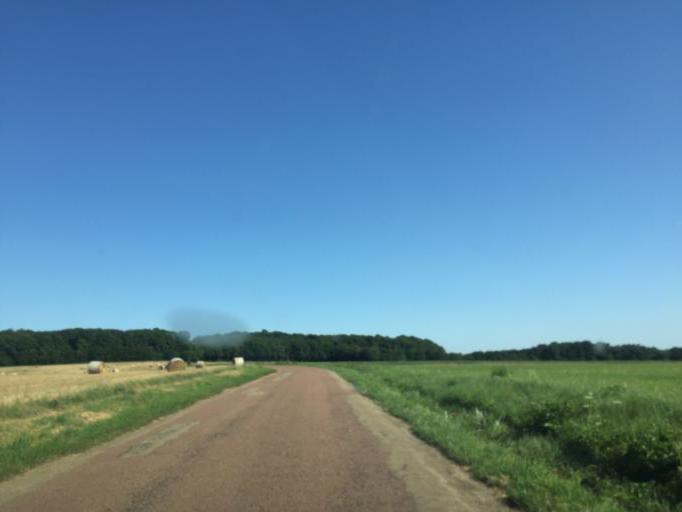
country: FR
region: Bourgogne
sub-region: Departement de l'Yonne
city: Fontenailles
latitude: 47.4898
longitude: 3.3746
